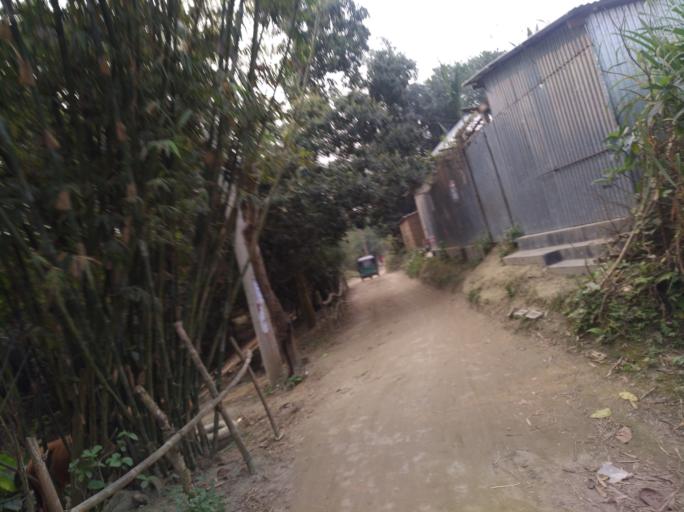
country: BD
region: Dhaka
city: Nagarpur
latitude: 24.0001
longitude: 89.8005
